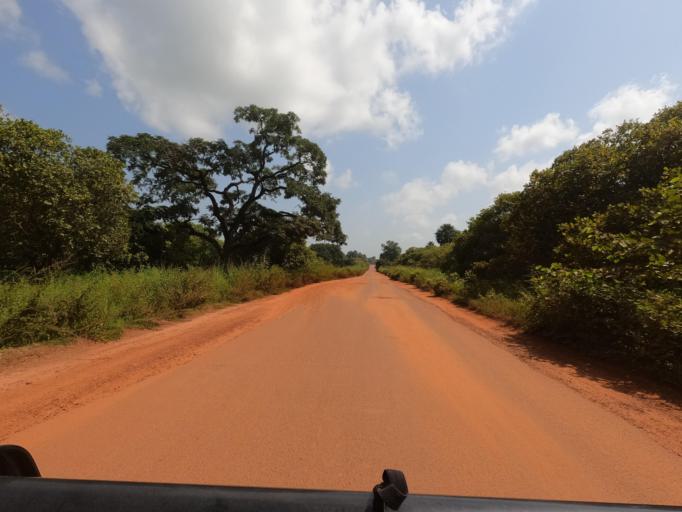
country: GW
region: Cacheu
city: Canchungo
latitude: 12.2859
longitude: -15.7795
